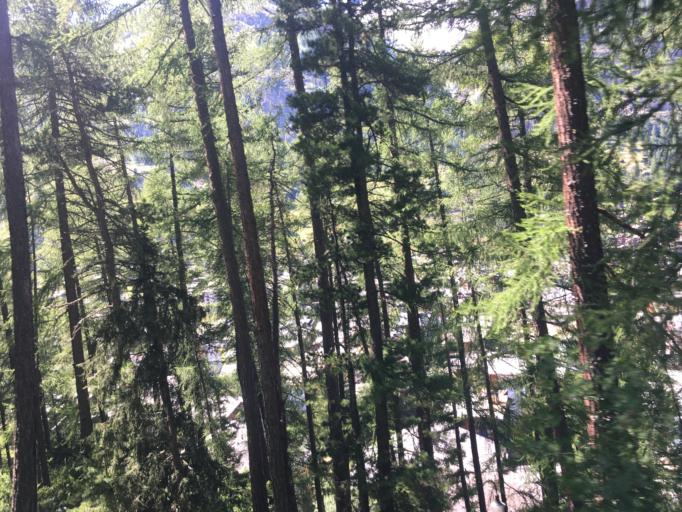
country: CH
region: Valais
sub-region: Visp District
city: Zermatt
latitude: 46.0170
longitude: 7.7510
